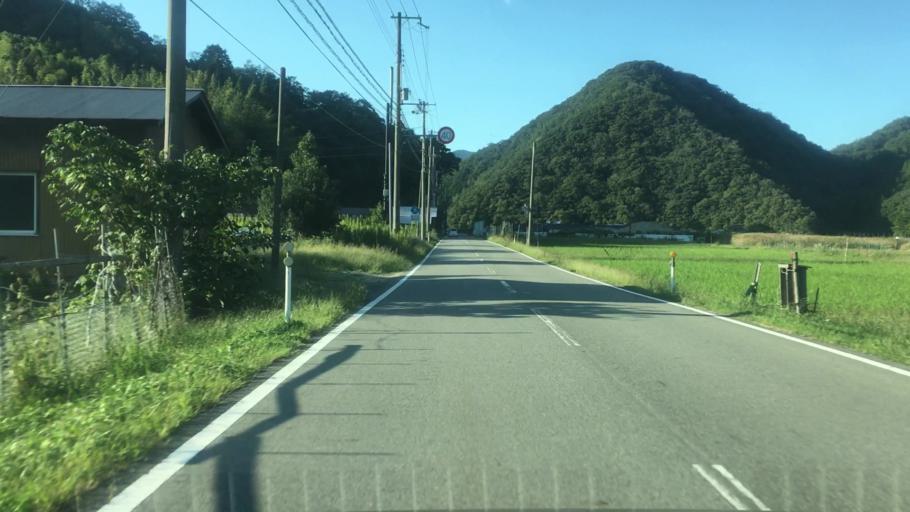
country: JP
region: Hyogo
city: Toyooka
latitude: 35.6129
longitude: 134.8279
